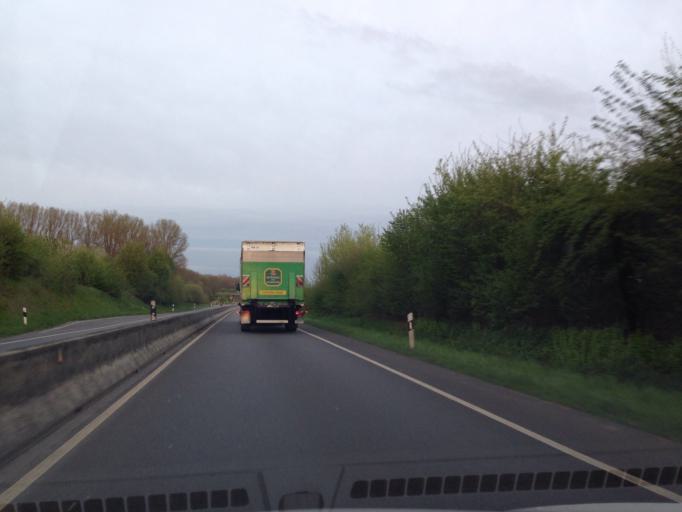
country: DE
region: North Rhine-Westphalia
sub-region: Regierungsbezirk Munster
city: Altenberge
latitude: 52.0375
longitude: 7.4655
